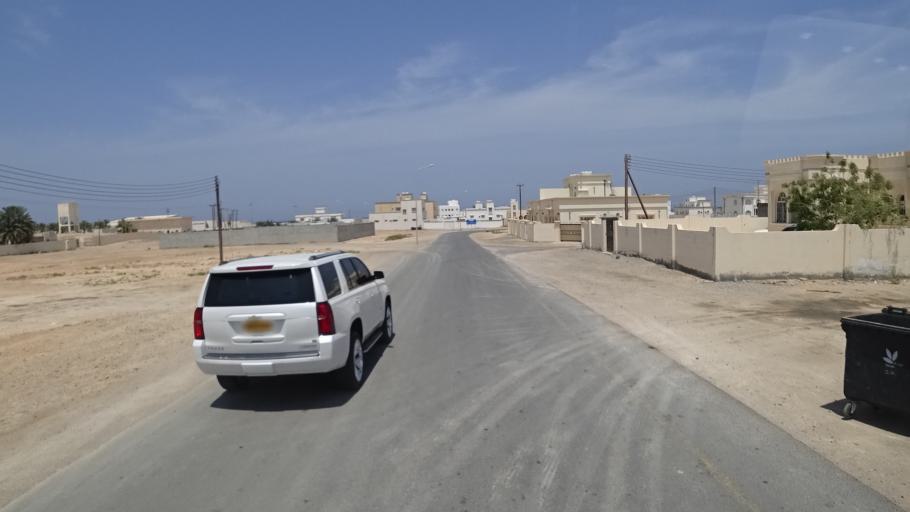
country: OM
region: Ash Sharqiyah
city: Sur
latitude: 22.6192
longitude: 59.4555
